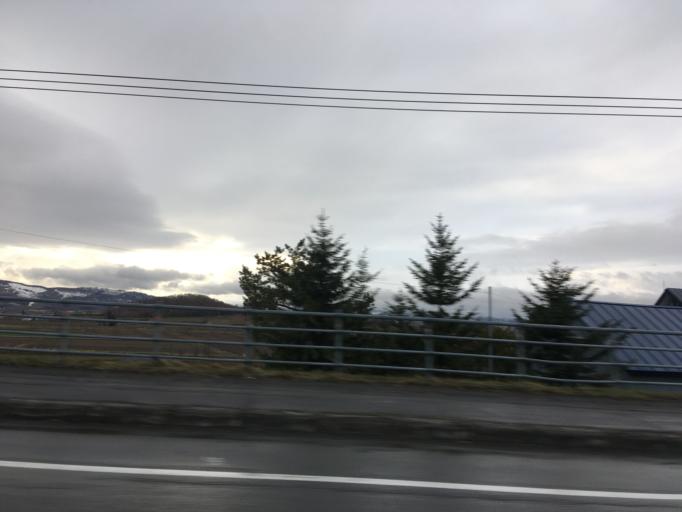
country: JP
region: Hokkaido
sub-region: Asahikawa-shi
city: Asahikawa
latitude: 44.0439
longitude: 142.4089
